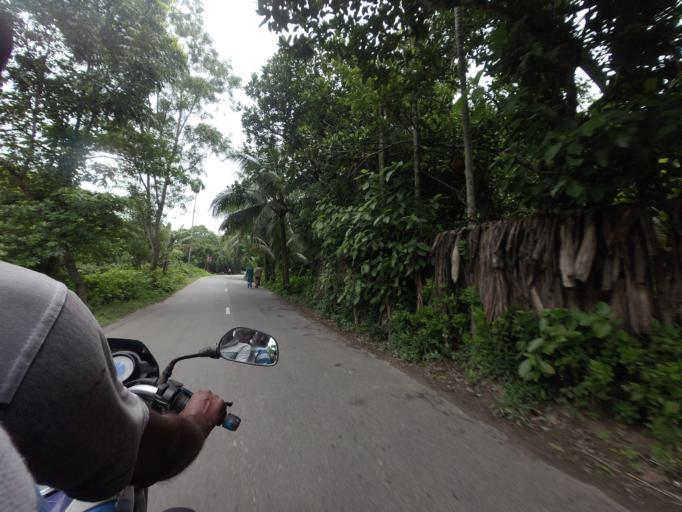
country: BD
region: Khulna
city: Kalia
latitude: 23.1669
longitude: 89.6455
